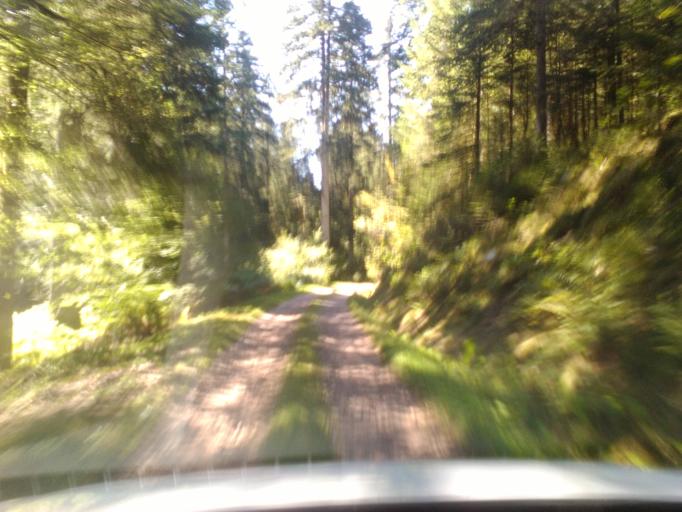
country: FR
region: Lorraine
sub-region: Departement des Vosges
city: Senones
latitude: 48.4269
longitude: 6.9540
